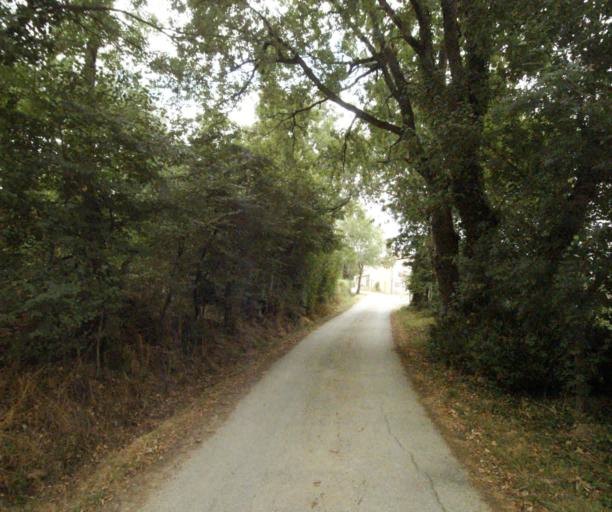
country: FR
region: Midi-Pyrenees
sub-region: Departement du Tarn
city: Soreze
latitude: 43.4780
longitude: 2.0438
